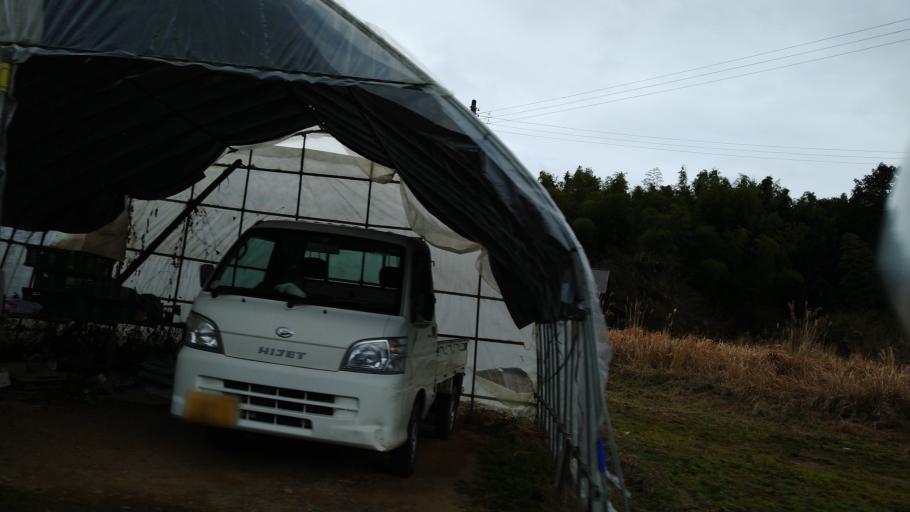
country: JP
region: Kyoto
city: Ayabe
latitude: 35.3234
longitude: 135.3590
